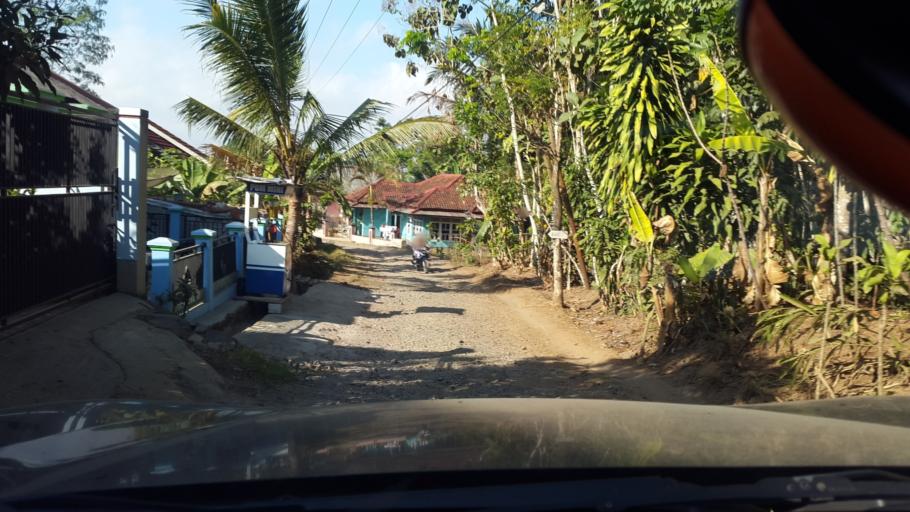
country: ID
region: West Java
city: Curugkembar Satu
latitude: -7.2183
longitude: 106.9391
